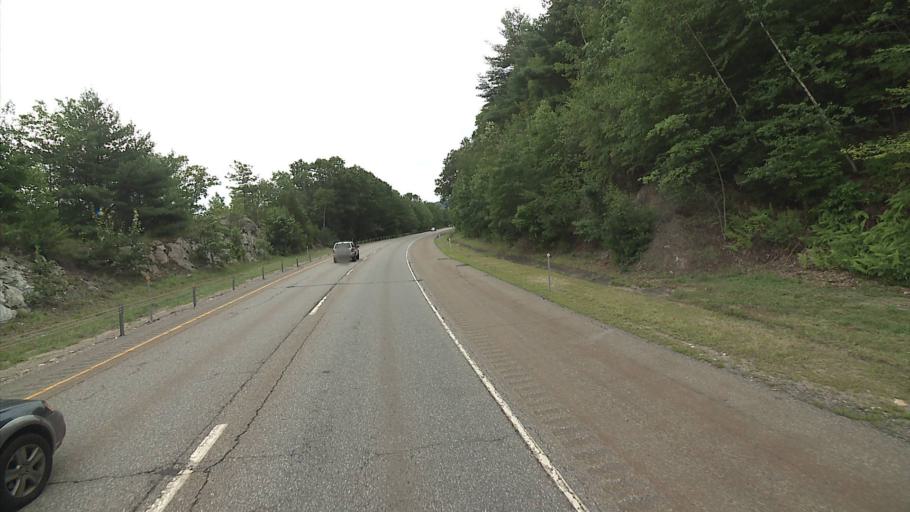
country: US
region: Connecticut
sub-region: Litchfield County
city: Thomaston
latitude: 41.7024
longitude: -73.0716
